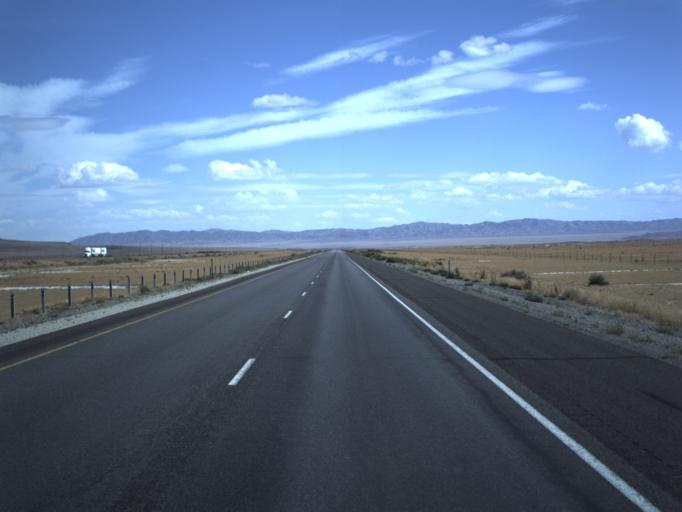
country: US
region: Utah
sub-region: Tooele County
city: Grantsville
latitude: 40.7260
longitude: -113.2187
